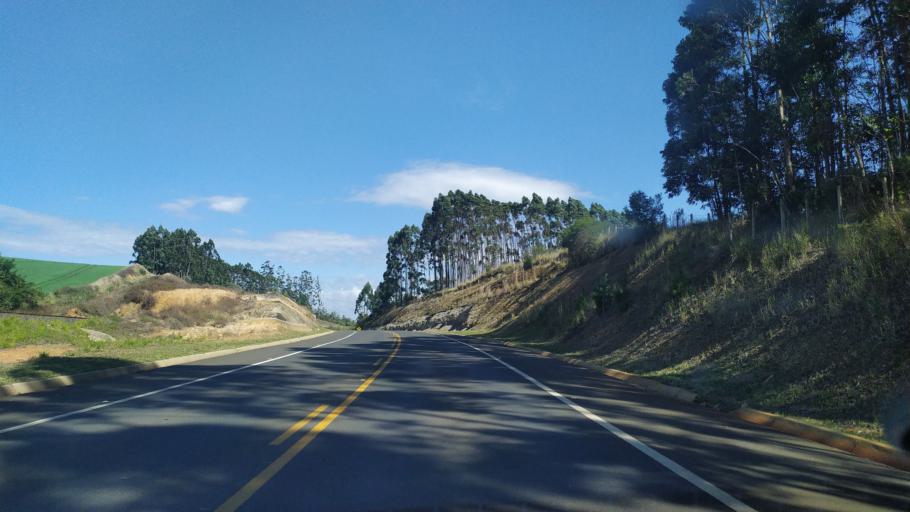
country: BR
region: Parana
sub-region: Ortigueira
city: Ortigueira
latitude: -24.2905
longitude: -50.8165
